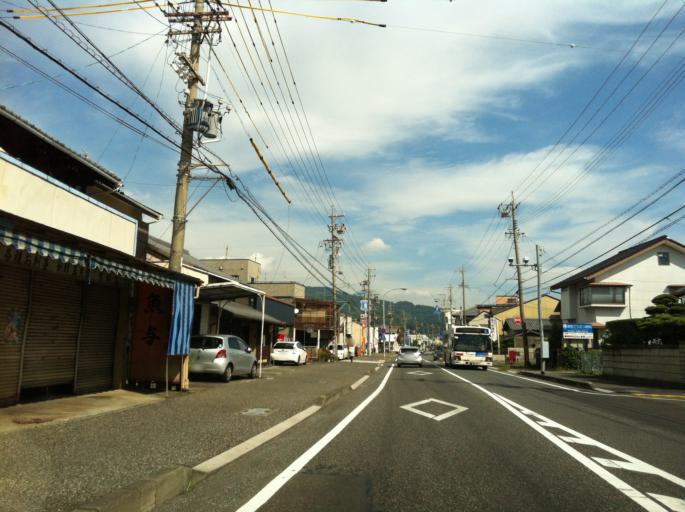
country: JP
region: Shizuoka
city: Shizuoka-shi
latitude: 35.0325
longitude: 138.4899
